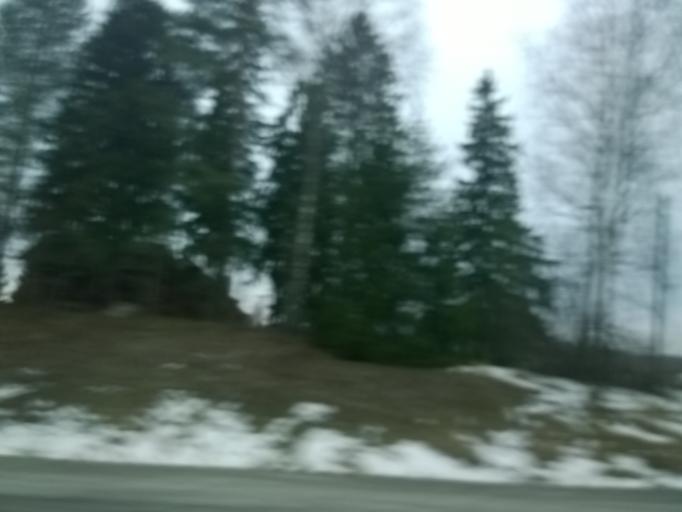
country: FI
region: Pirkanmaa
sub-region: Tampere
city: Lempaeaelae
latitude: 61.3232
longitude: 23.7703
